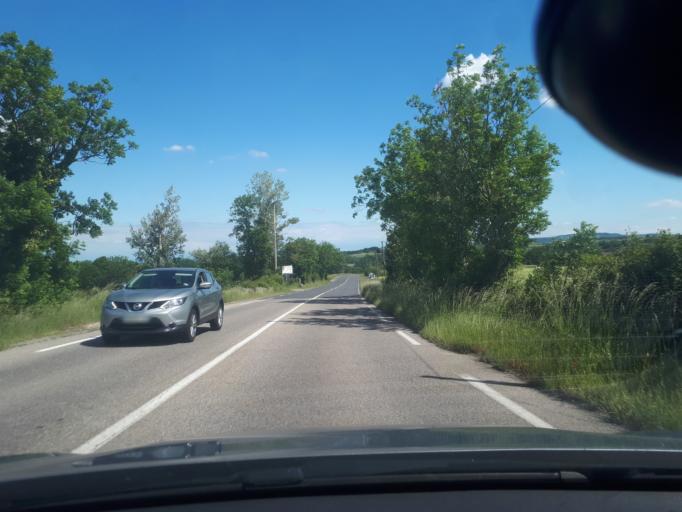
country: FR
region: Rhone-Alpes
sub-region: Departement du Rhone
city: Mornant
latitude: 45.6082
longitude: 4.6824
